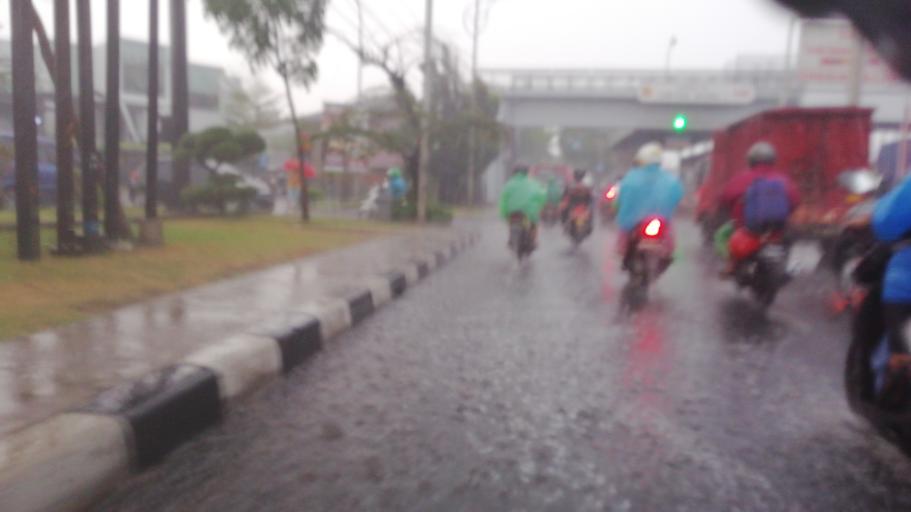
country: ID
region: Jakarta Raya
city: Jakarta
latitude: -6.3039
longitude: 106.8480
